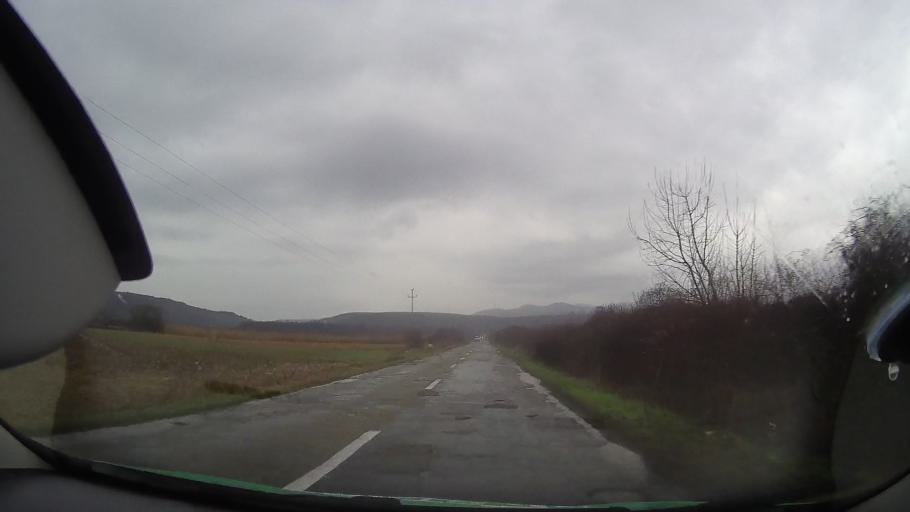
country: RO
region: Bihor
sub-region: Comuna Soimi
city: Soimi
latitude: 46.6918
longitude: 22.0998
